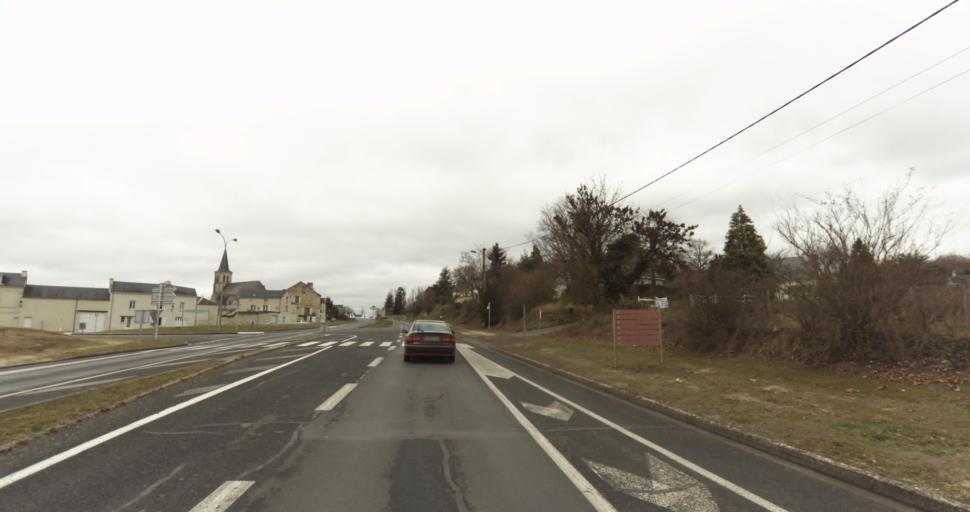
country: FR
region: Pays de la Loire
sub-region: Departement de Maine-et-Loire
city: Varrains
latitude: 47.2252
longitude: -0.0649
